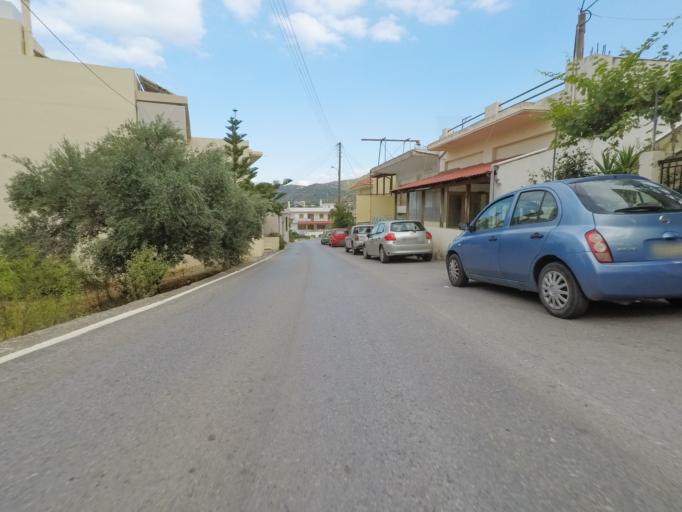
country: GR
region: Crete
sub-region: Nomos Lasithiou
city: Kritsa
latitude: 35.1557
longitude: 25.6473
